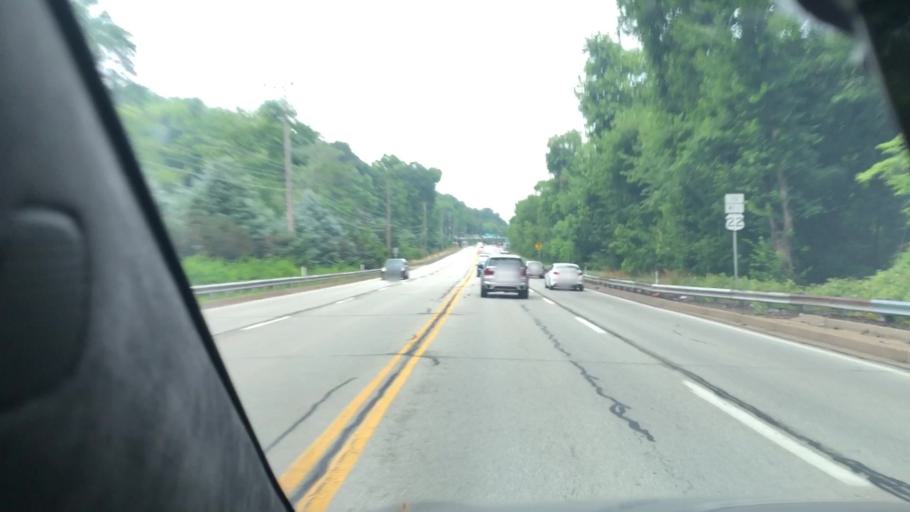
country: US
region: Pennsylvania
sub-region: Allegheny County
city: Churchill
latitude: 40.4360
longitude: -79.8258
